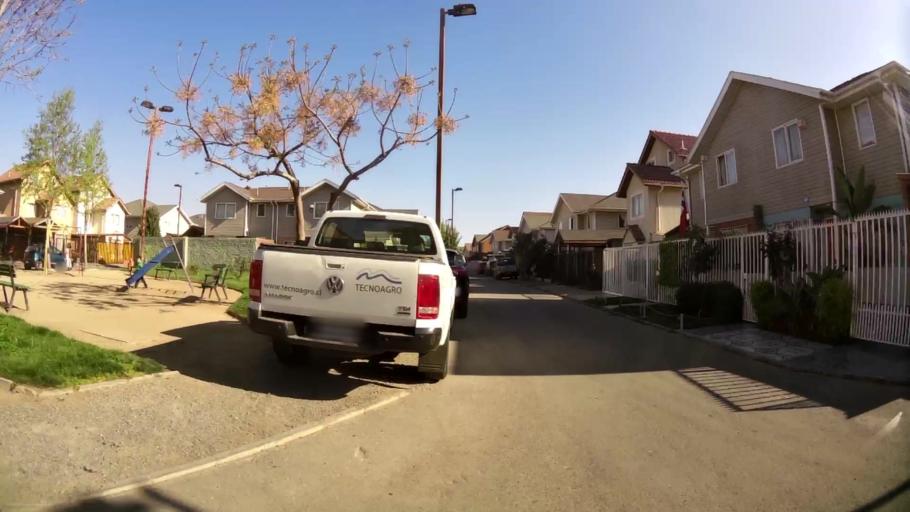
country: CL
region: Santiago Metropolitan
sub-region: Provincia de Santiago
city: Lo Prado
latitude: -33.4920
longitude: -70.7819
